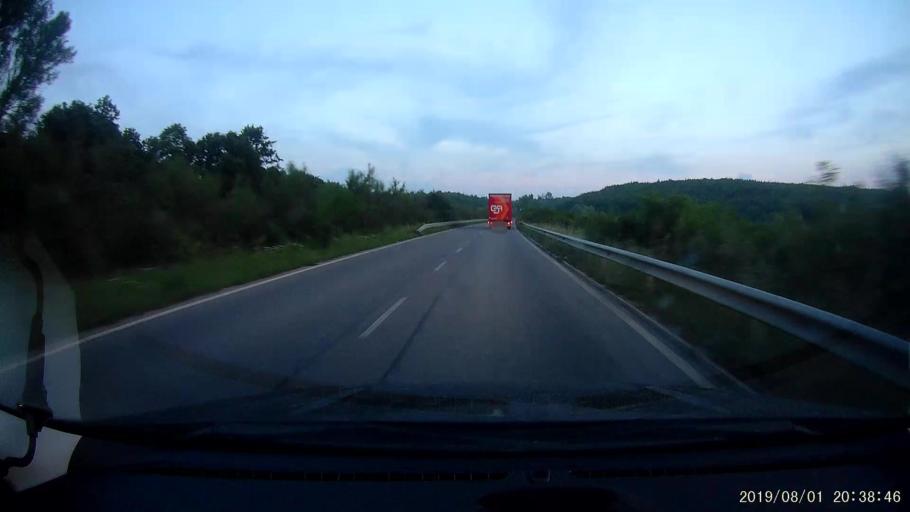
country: BG
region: Yambol
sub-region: Obshtina Elkhovo
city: Elkhovo
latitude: 42.0188
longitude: 26.6014
